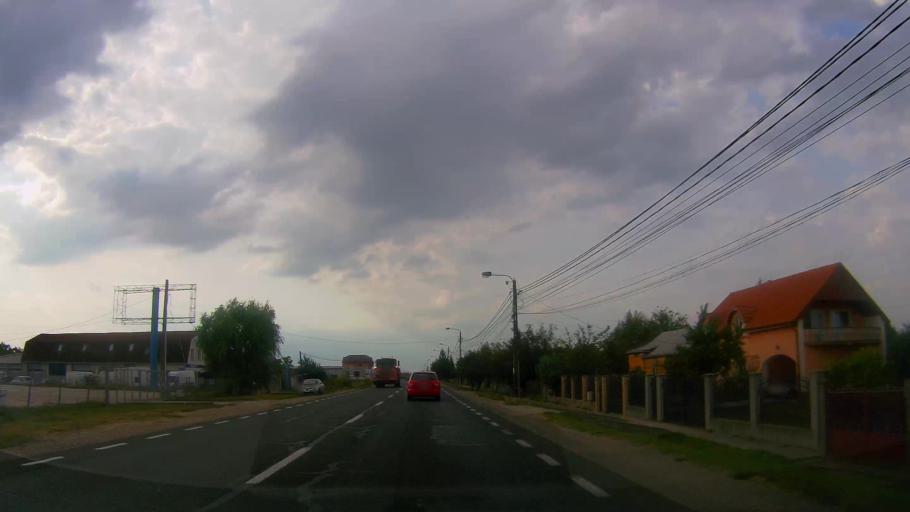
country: RO
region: Satu Mare
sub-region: Comuna Paulesti
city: Paulesti
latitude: 47.7550
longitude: 22.8831
